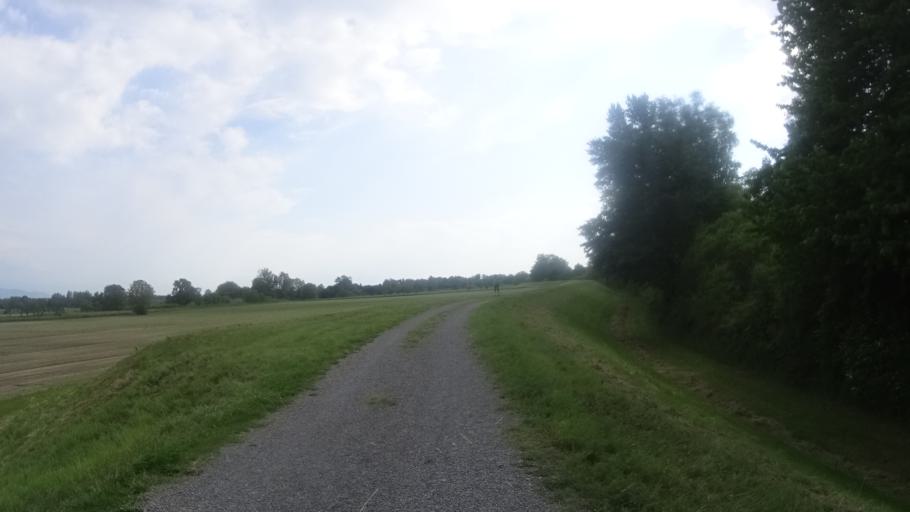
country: DE
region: Baden-Wuerttemberg
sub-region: Karlsruhe Region
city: Hugelsheim
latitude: 48.8020
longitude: 8.0949
